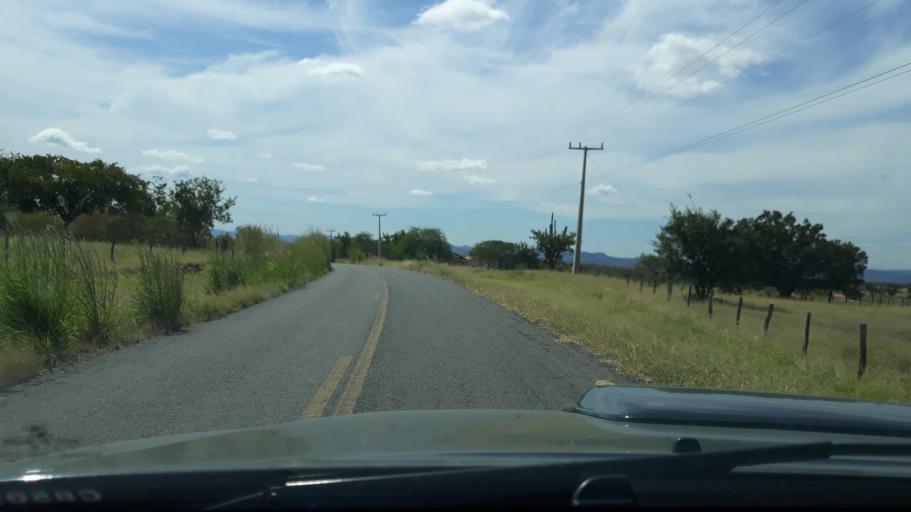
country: BR
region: Bahia
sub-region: Guanambi
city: Guanambi
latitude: -14.0494
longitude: -42.8736
